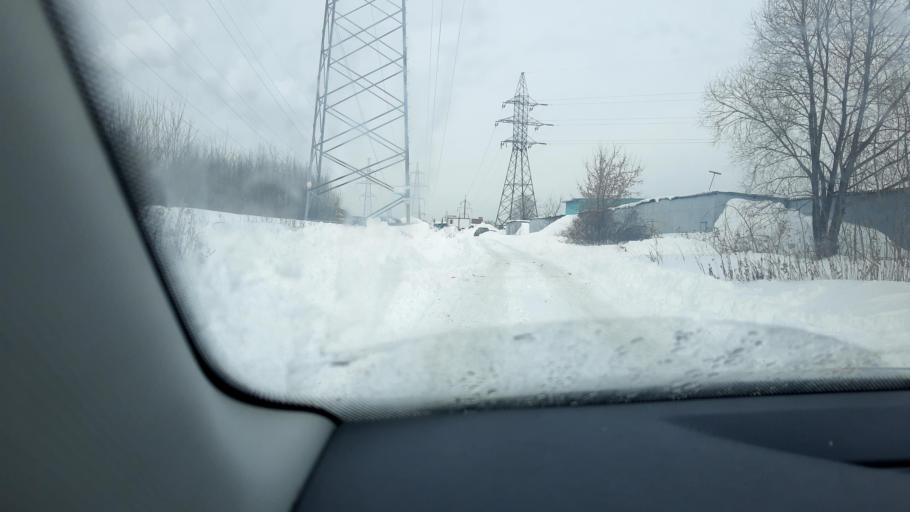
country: RU
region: Moskovskaya
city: Biryulevo Zapadnoye
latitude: 55.5968
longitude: 37.6392
